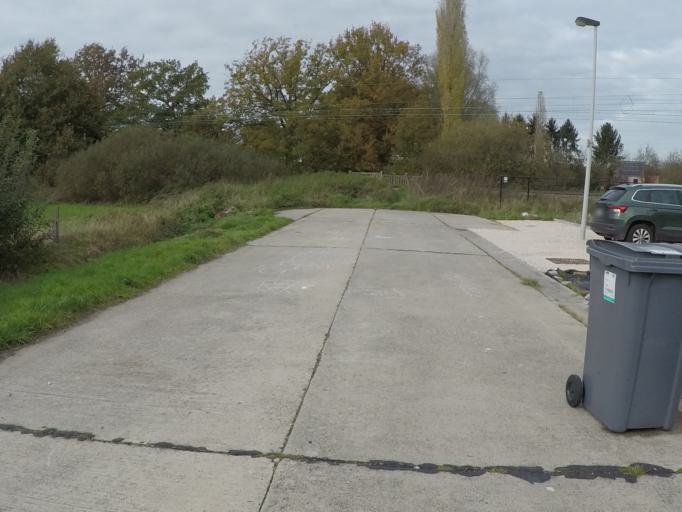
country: BE
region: Flanders
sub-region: Provincie Antwerpen
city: Nijlen
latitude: 51.1581
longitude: 4.6497
